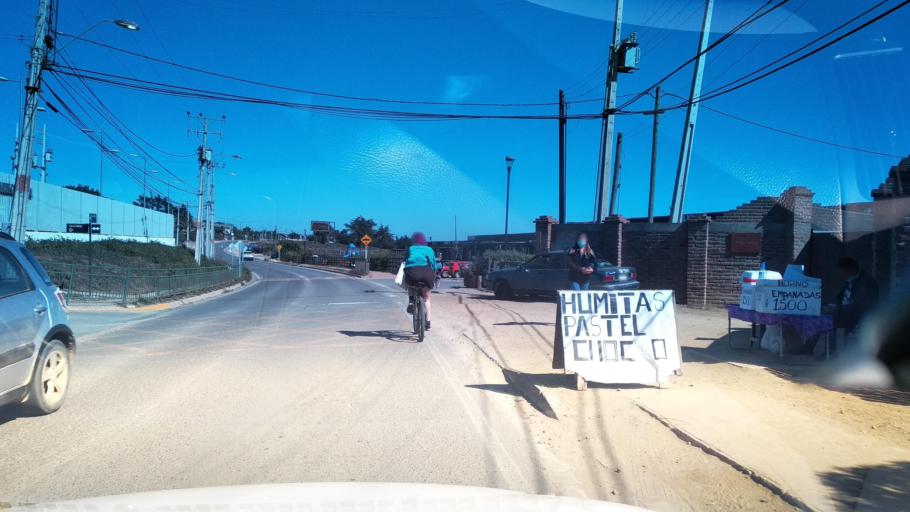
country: CL
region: O'Higgins
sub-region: Provincia de Colchagua
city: Santa Cruz
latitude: -34.4050
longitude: -72.0256
